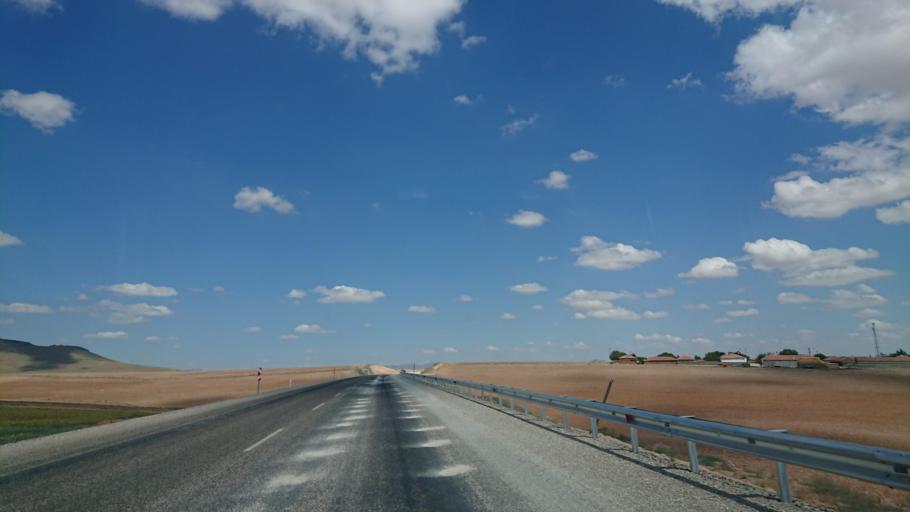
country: TR
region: Kirsehir
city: Kirsehir
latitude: 39.1238
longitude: 33.9824
